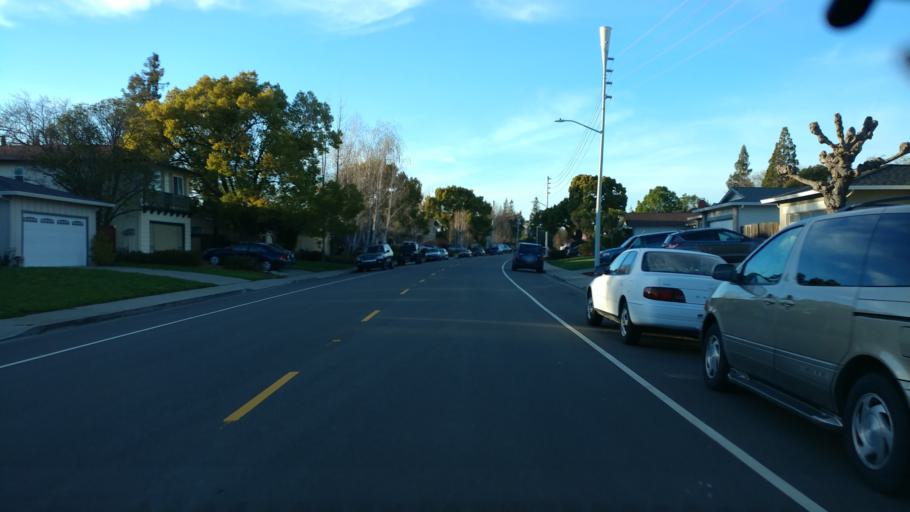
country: US
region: California
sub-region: Contra Costa County
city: San Ramon
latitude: 37.7438
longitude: -121.9532
